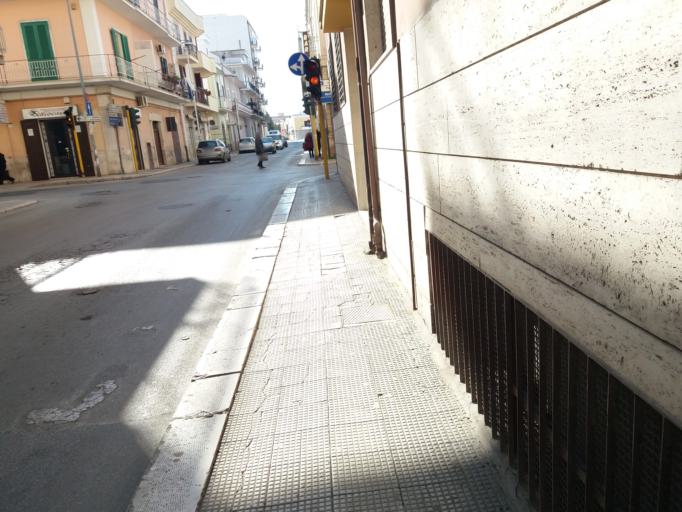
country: IT
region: Apulia
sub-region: Provincia di Bari
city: Bitonto
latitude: 41.1103
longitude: 16.6838
